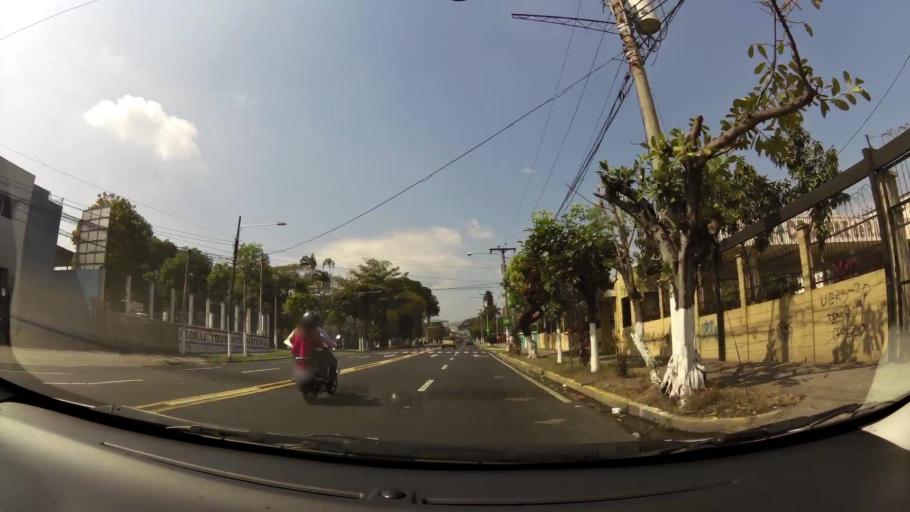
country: SV
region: San Salvador
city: San Salvador
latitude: 13.7000
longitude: -89.2102
